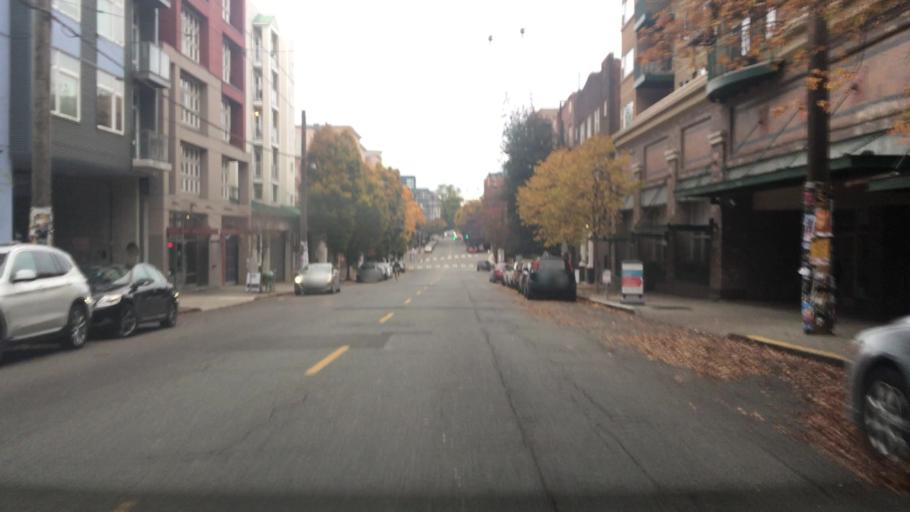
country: US
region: Washington
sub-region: King County
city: Seattle
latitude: 47.6156
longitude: -122.3268
